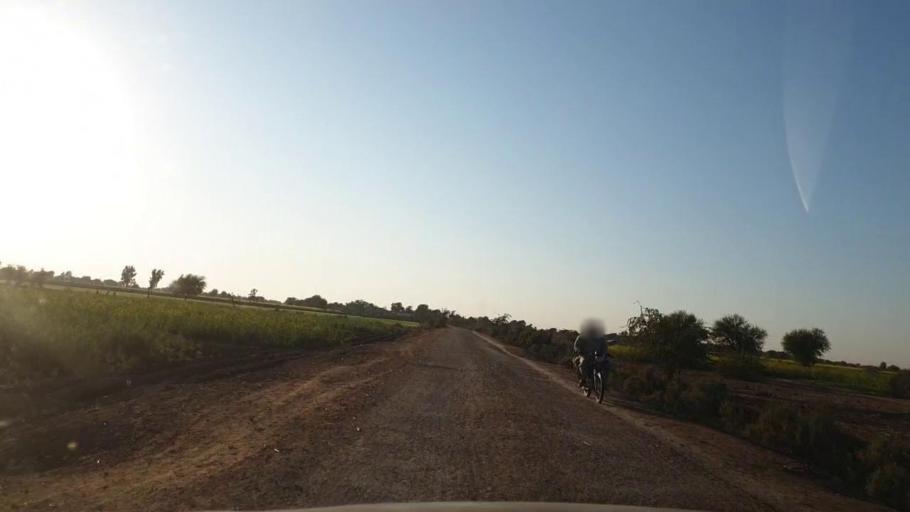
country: PK
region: Sindh
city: Jhol
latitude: 25.8808
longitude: 68.9067
